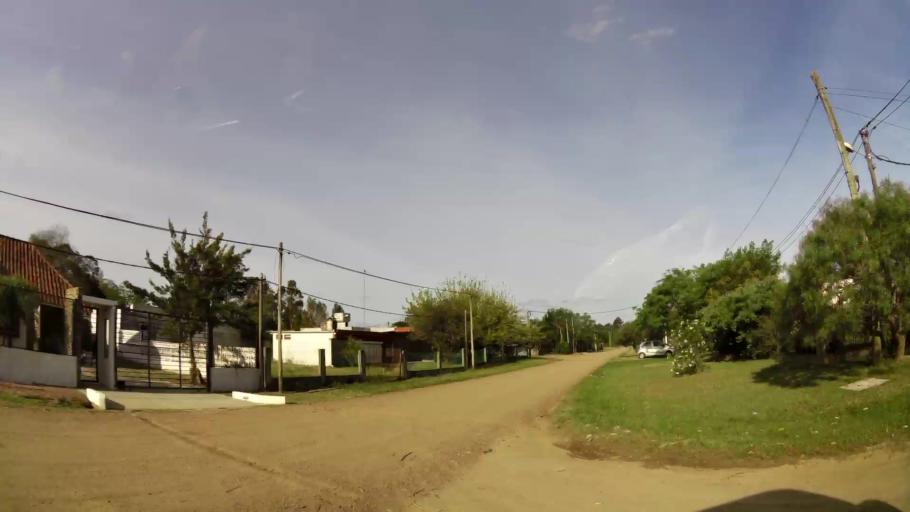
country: UY
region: Canelones
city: Atlantida
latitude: -34.7858
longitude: -55.8481
